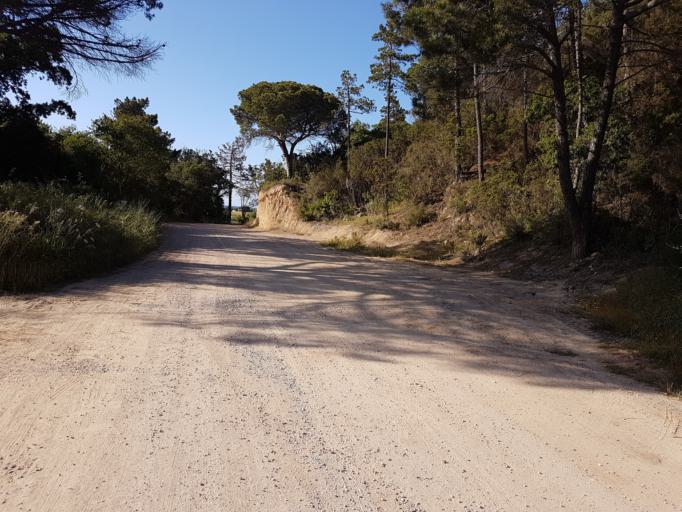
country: IT
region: Tuscany
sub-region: Provincia di Livorno
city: Portoferraio
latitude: 42.7908
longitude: 10.3512
